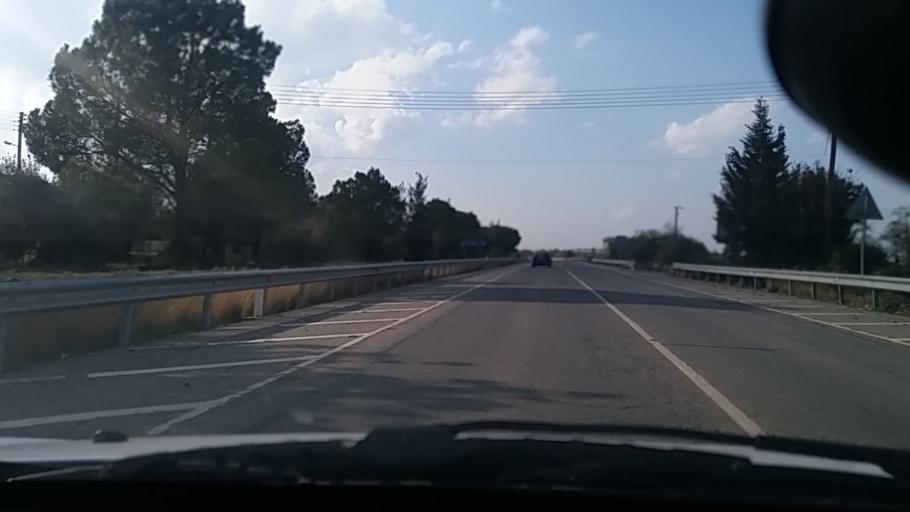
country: CY
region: Lefkosia
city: Kokkinotrimithia
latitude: 35.1471
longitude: 33.1844
